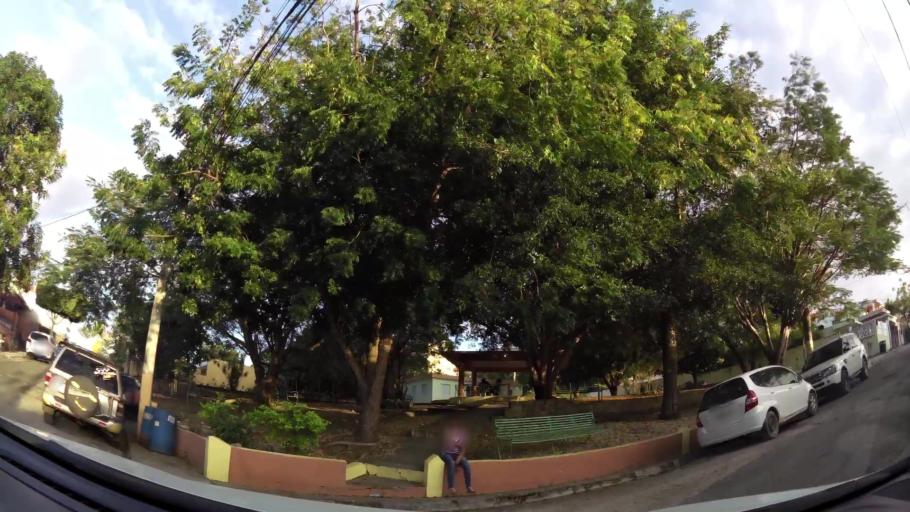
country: DO
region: Nacional
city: La Agustina
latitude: 18.5554
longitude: -69.9246
